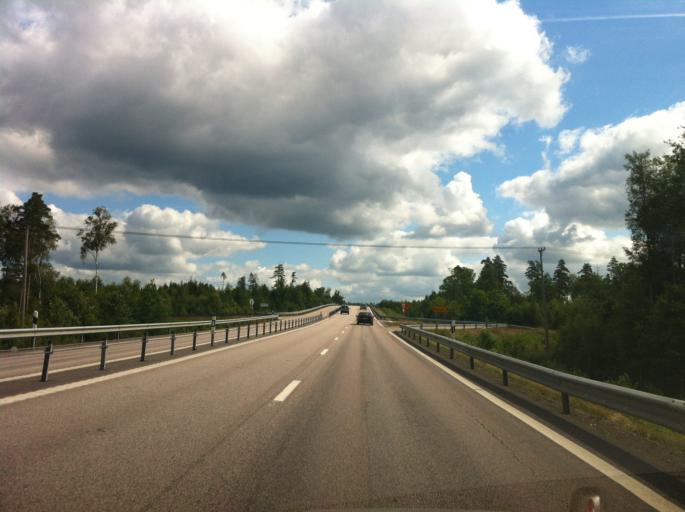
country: SE
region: Halland
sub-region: Hylte Kommun
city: Torup
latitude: 56.9591
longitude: 13.0924
